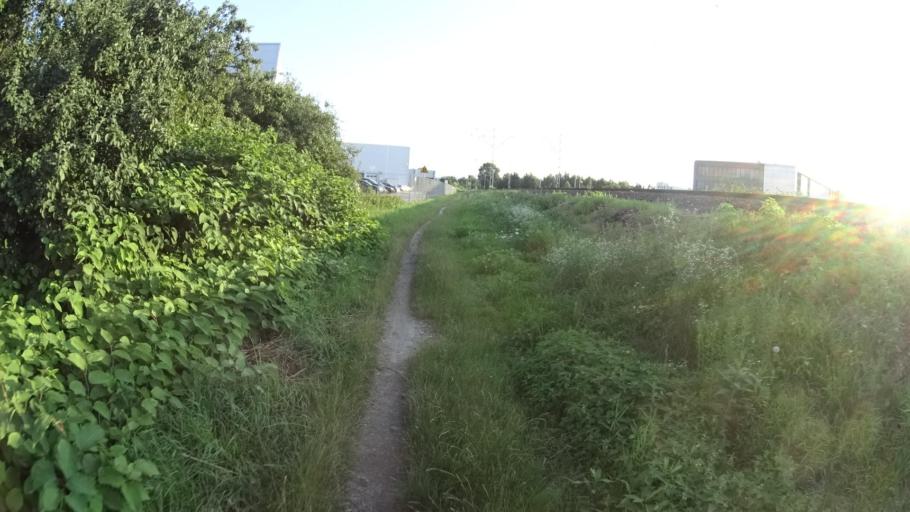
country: PL
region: Masovian Voivodeship
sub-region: Warszawa
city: Wlochy
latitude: 52.1902
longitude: 20.9306
